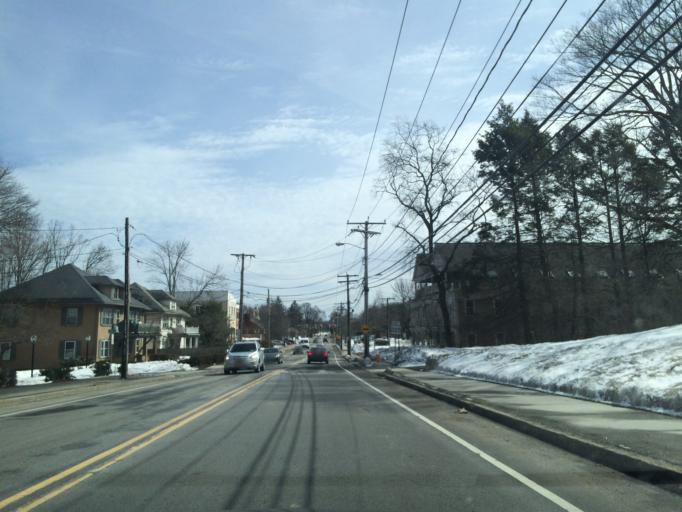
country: US
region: Massachusetts
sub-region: Middlesex County
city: Lexington
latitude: 42.4546
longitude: -71.2338
